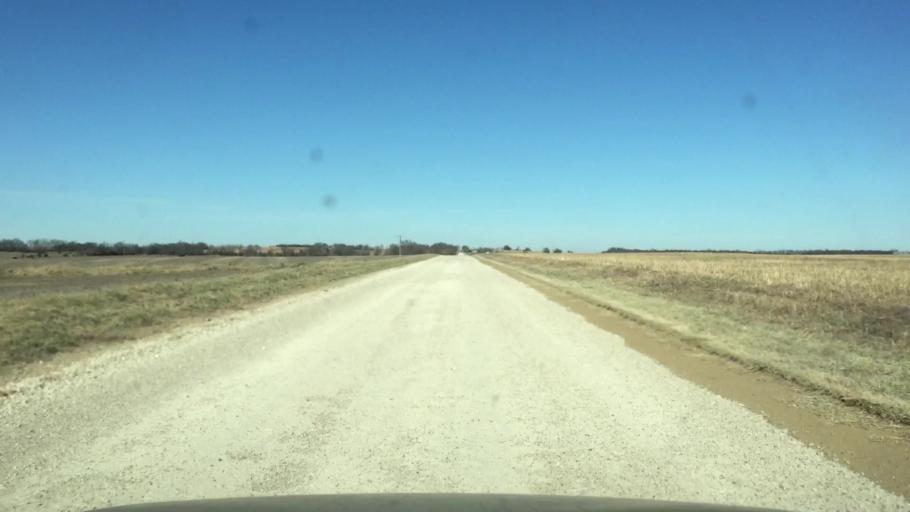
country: US
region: Kansas
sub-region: Allen County
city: Iola
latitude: 37.8611
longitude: -95.3910
